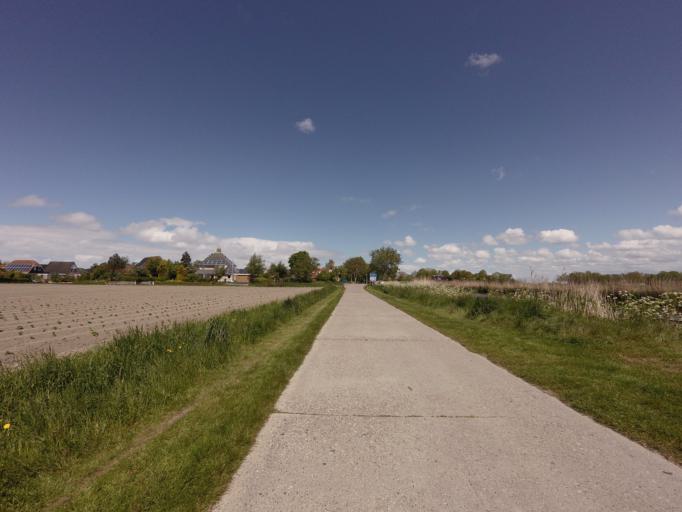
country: NL
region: Friesland
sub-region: Gemeente Harlingen
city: Harlingen
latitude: 53.1384
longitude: 5.4358
